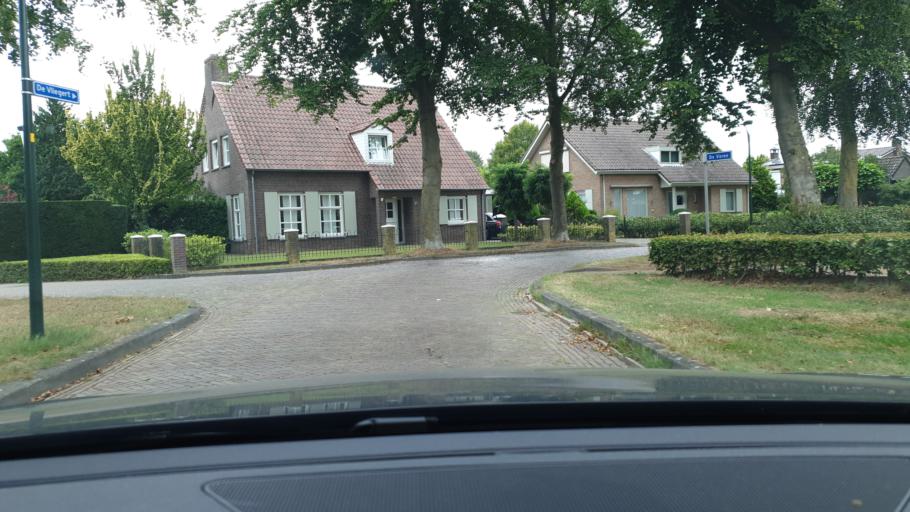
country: NL
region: North Brabant
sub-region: Gemeente Bladel en Netersel
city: Bladel
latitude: 51.3695
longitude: 5.2462
